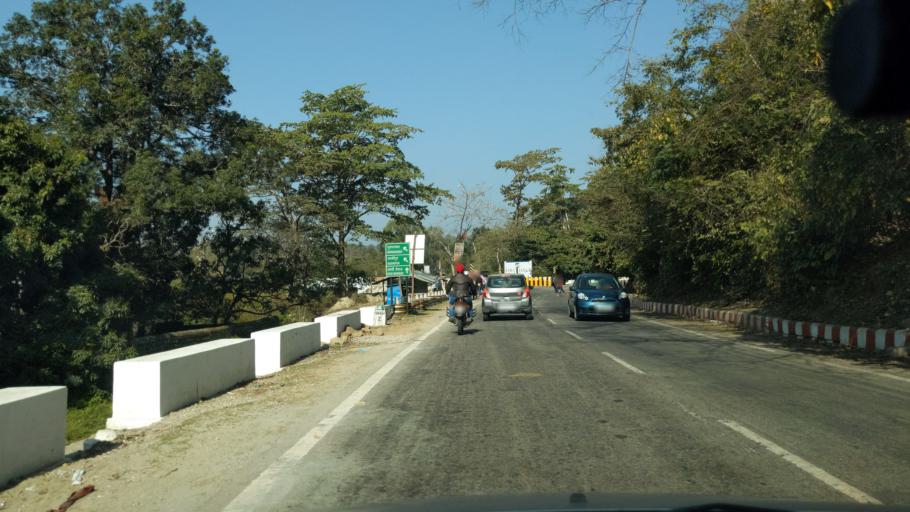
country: IN
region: Uttarakhand
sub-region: Naini Tal
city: Ramnagar
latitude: 29.3902
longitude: 79.1384
